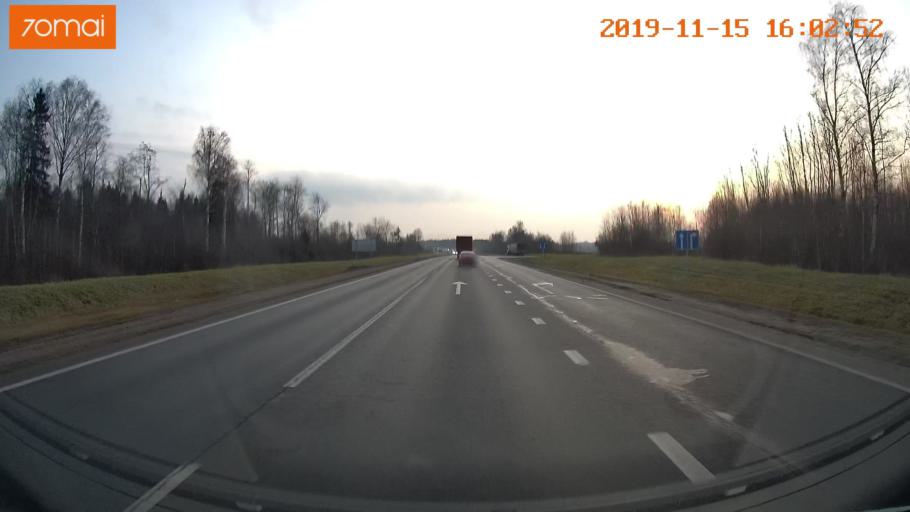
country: RU
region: Jaroslavl
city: Yaroslavl
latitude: 57.7667
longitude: 39.9201
